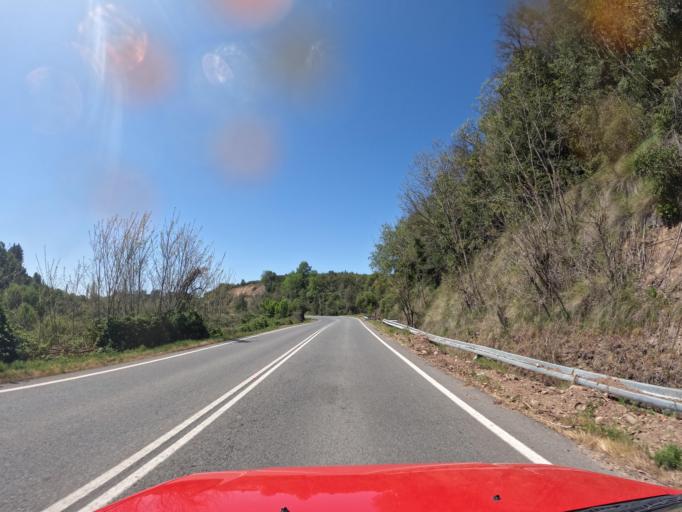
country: CL
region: Maule
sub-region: Provincia de Talca
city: San Clemente
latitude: -35.4667
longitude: -71.2719
